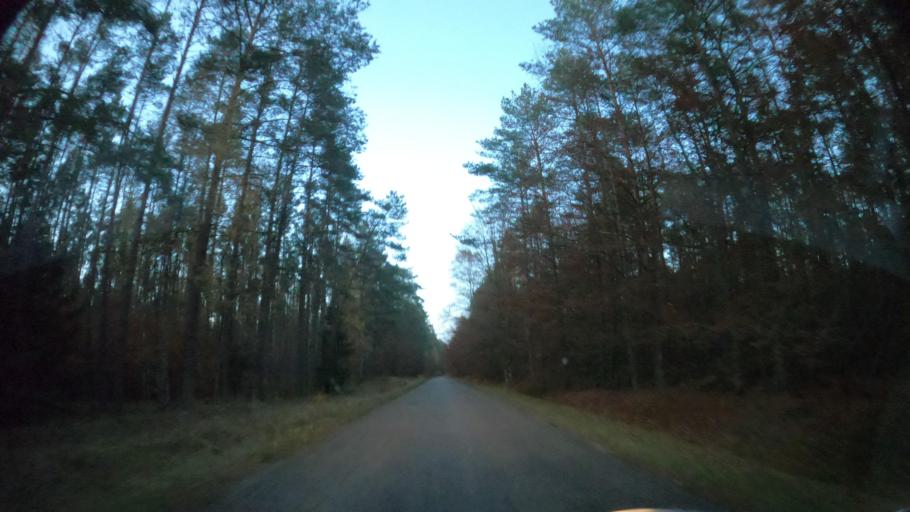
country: PL
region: Greater Poland Voivodeship
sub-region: Powiat zlotowski
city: Sypniewo
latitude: 53.3981
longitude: 16.5778
